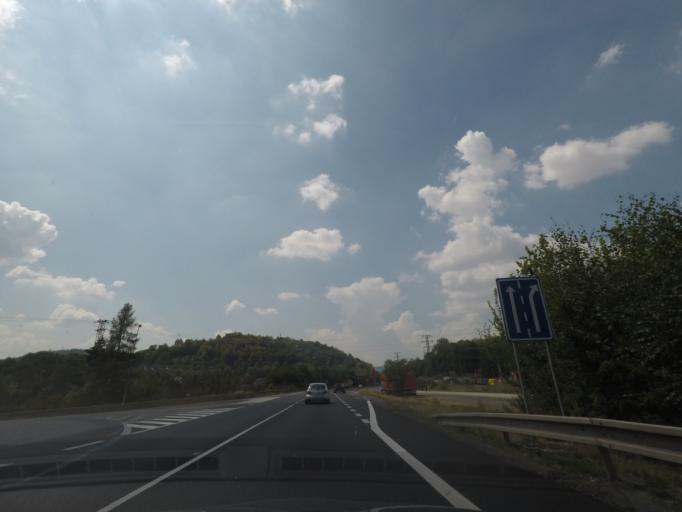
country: CZ
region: Pardubicky
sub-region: Okres Svitavy
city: Moravska Trebova
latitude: 49.7611
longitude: 16.6828
